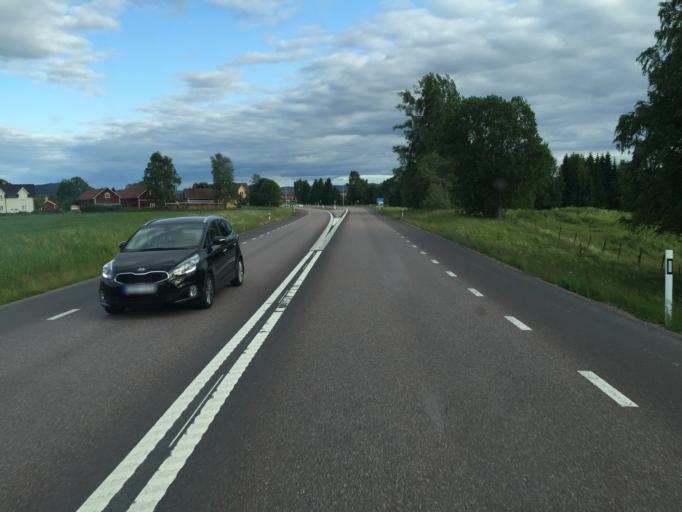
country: SE
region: Dalarna
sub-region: Gagnefs Kommun
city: Gagnef
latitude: 60.5925
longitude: 15.0836
